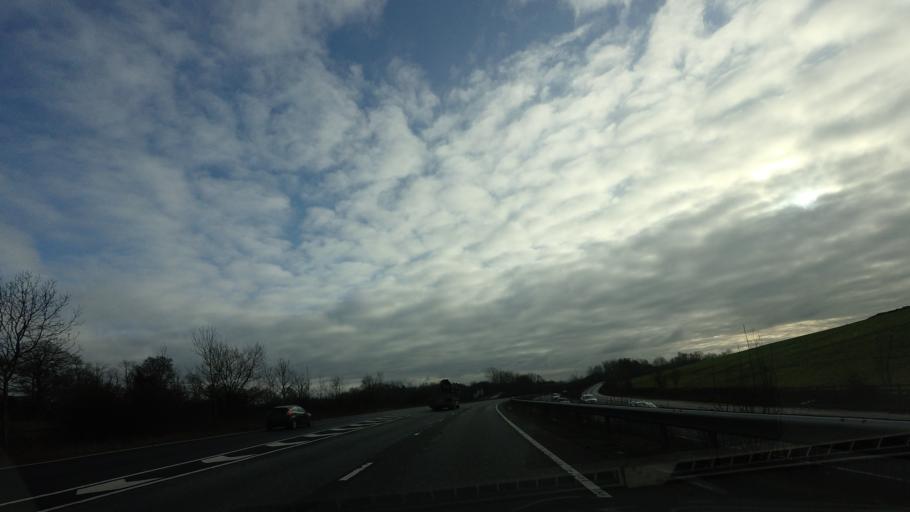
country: GB
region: England
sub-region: Kent
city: Sevenoaks
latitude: 51.2427
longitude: 0.2057
